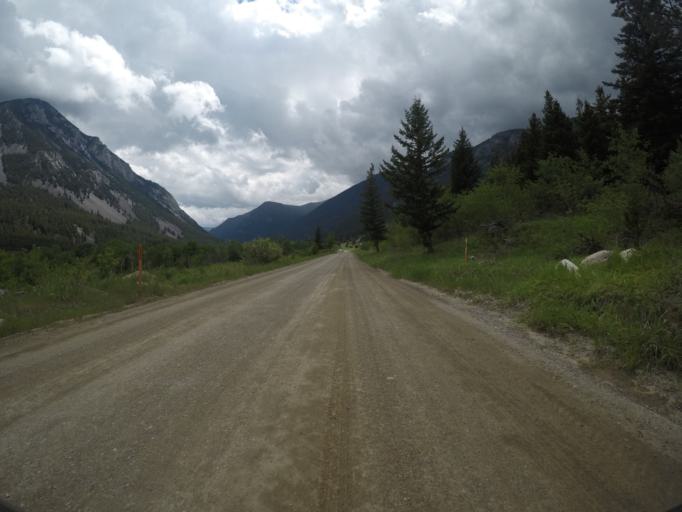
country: US
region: Montana
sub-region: Park County
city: Livingston
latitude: 45.5204
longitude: -110.2252
